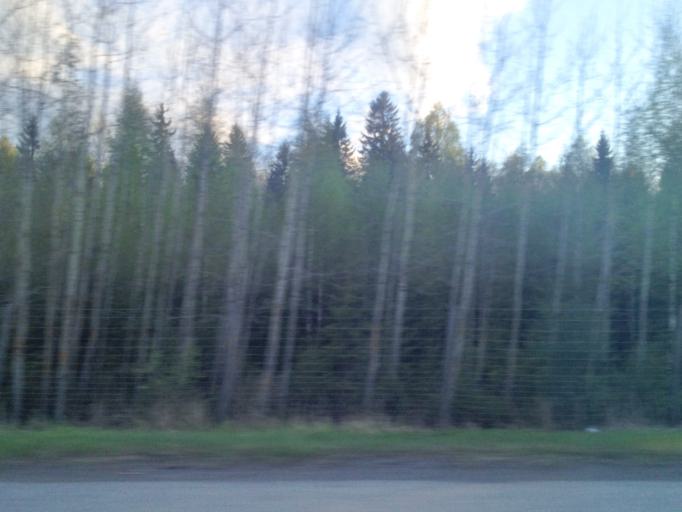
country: FI
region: Haeme
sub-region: Haemeenlinna
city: Tervakoski
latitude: 60.8044
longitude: 24.6816
